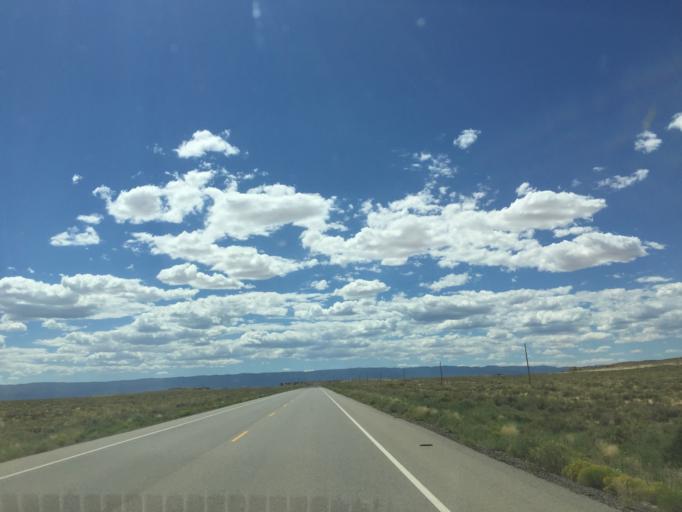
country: US
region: New Mexico
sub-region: San Juan County
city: Waterflow
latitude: 36.3522
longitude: -108.6246
